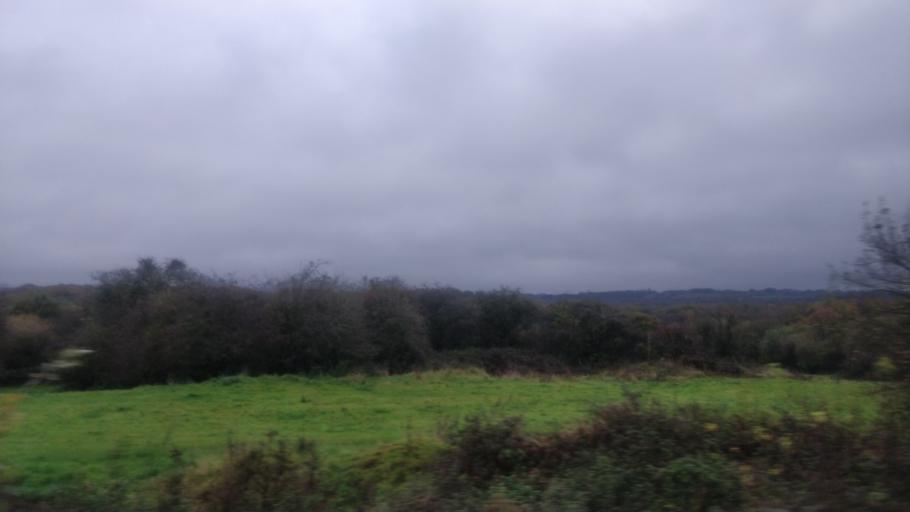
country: GB
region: England
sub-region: Borough of Wigan
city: Shevington
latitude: 53.5583
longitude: -2.6851
